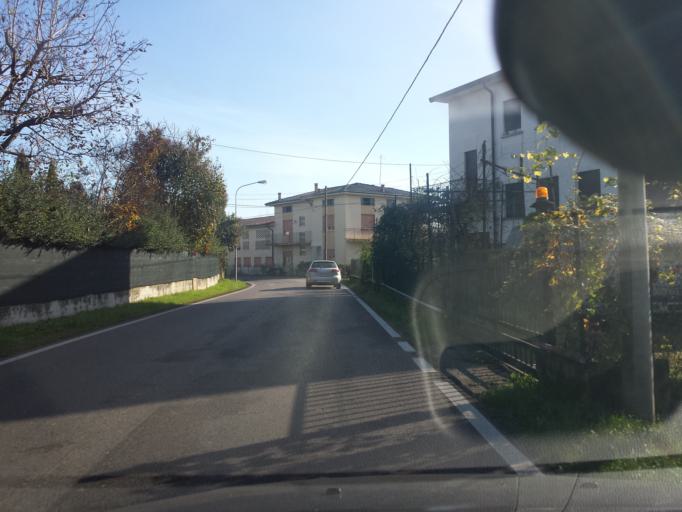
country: IT
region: Veneto
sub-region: Provincia di Vicenza
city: Caldogno-Rettorgole-Cresole
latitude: 45.6106
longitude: 11.5201
